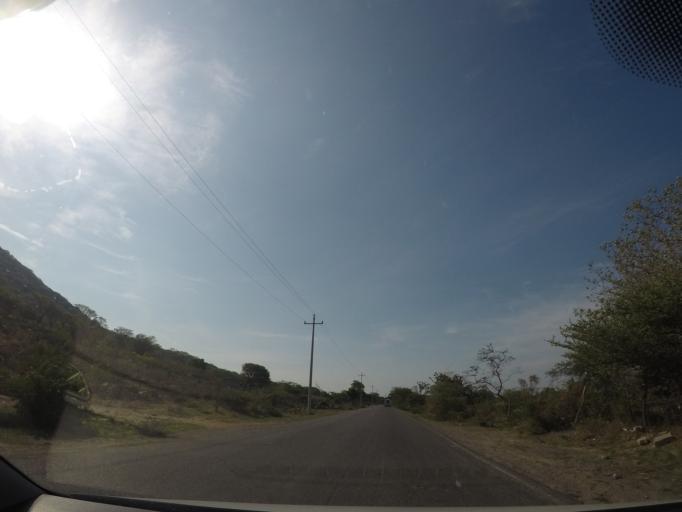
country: MX
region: Oaxaca
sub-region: Santo Domingo Tehuantepec
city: La Noria
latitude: 16.2355
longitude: -95.1525
